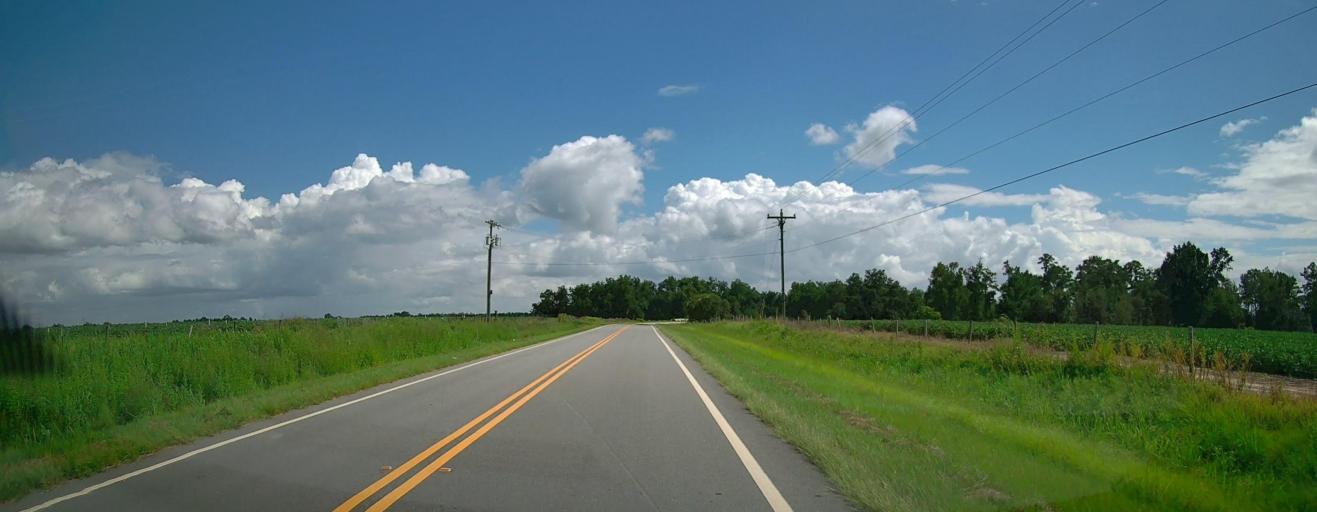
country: US
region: Georgia
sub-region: Irwin County
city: Ocilla
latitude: 31.6035
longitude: -83.1657
